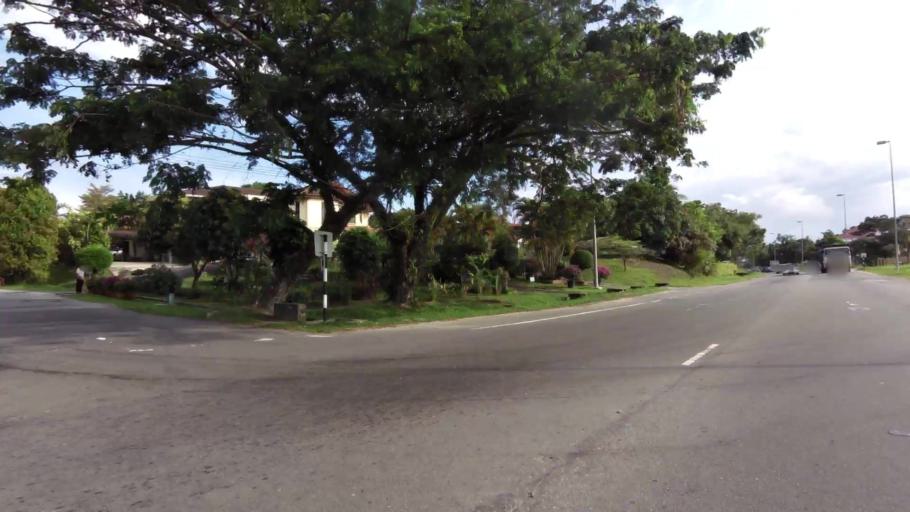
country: BN
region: Brunei and Muara
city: Bandar Seri Begawan
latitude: 4.9700
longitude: 114.9790
